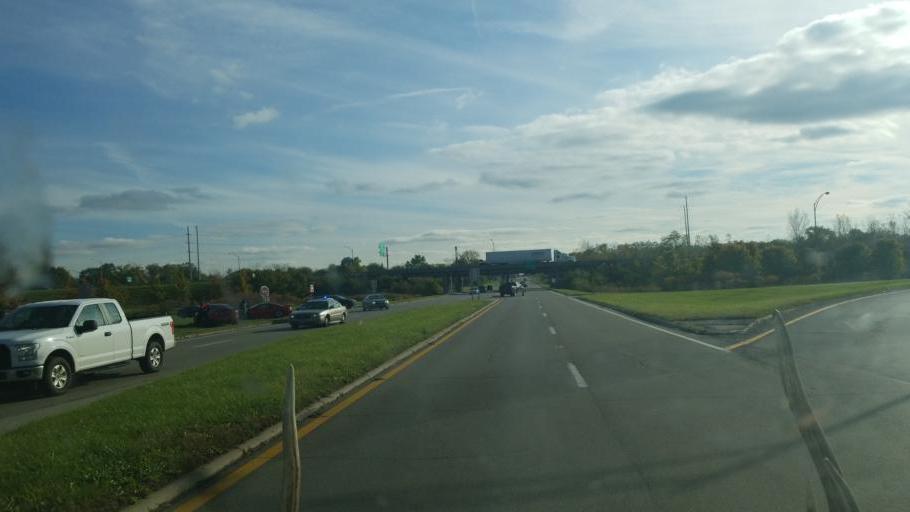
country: US
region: Ohio
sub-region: Clark County
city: Springfield
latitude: 39.8936
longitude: -83.8117
